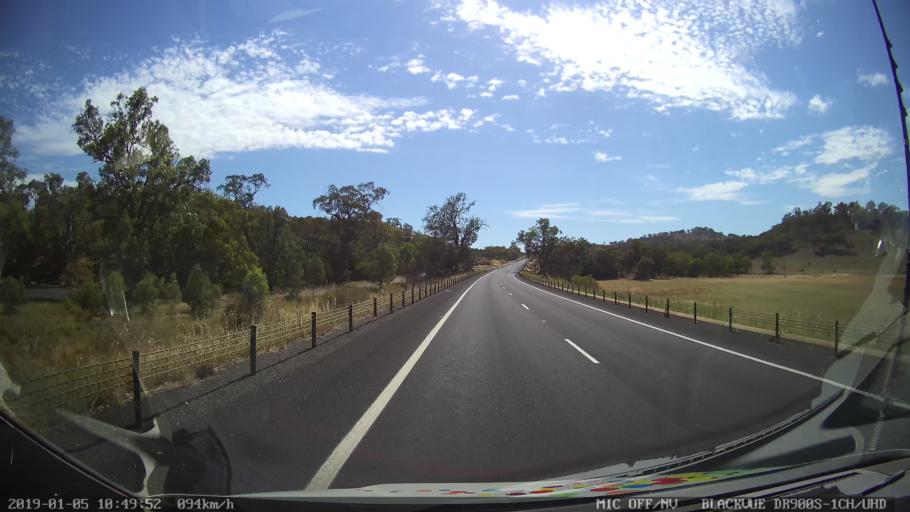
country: AU
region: New South Wales
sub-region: Warrumbungle Shire
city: Coonabarabran
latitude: -31.4311
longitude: 149.0668
